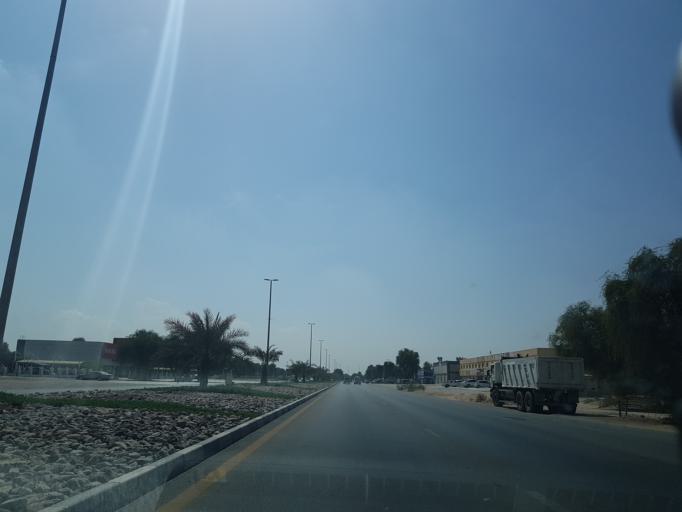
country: AE
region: Ra's al Khaymah
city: Ras al-Khaimah
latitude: 25.7093
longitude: 55.9698
